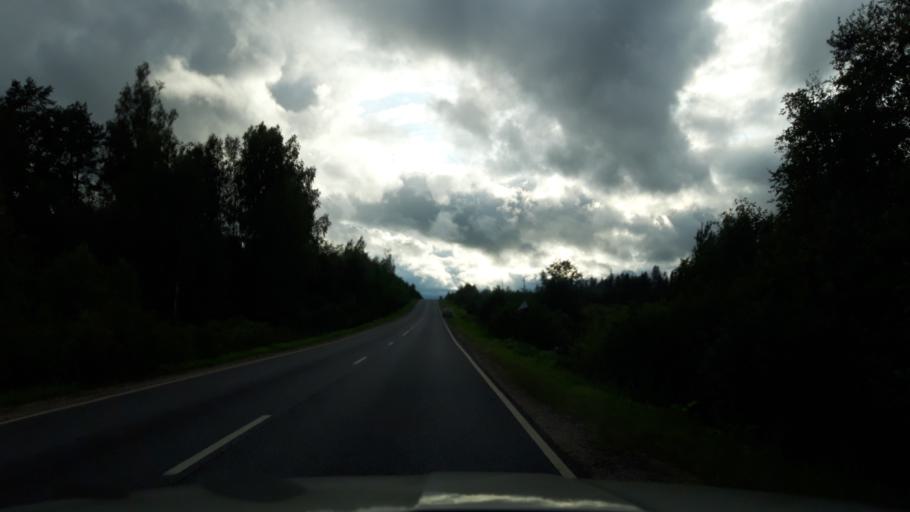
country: RU
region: Moskovskaya
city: Solnechnogorsk
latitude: 56.0939
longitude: 36.8383
